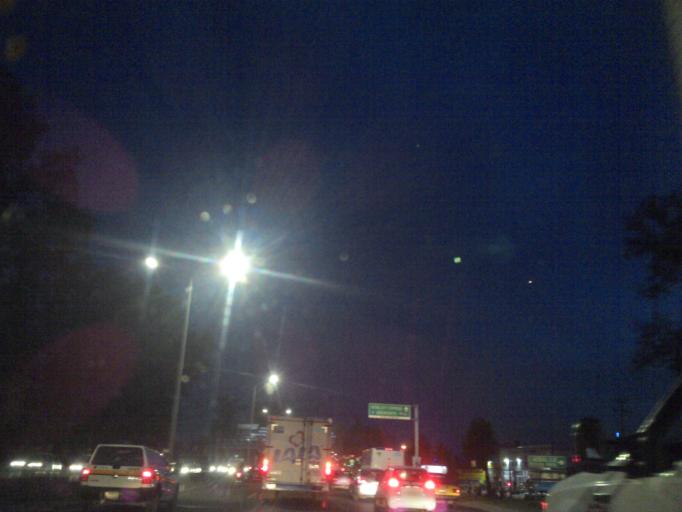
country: MX
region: Jalisco
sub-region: San Pedro Tlaquepaque
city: Paseo del Prado
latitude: 20.5991
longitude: -103.3932
